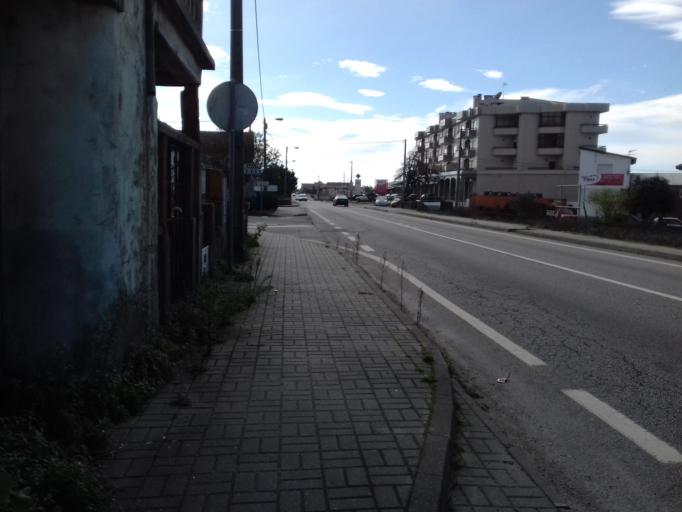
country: PT
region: Aveiro
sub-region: Albergaria-A-Velha
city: Branca
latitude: 40.7638
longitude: -8.4826
